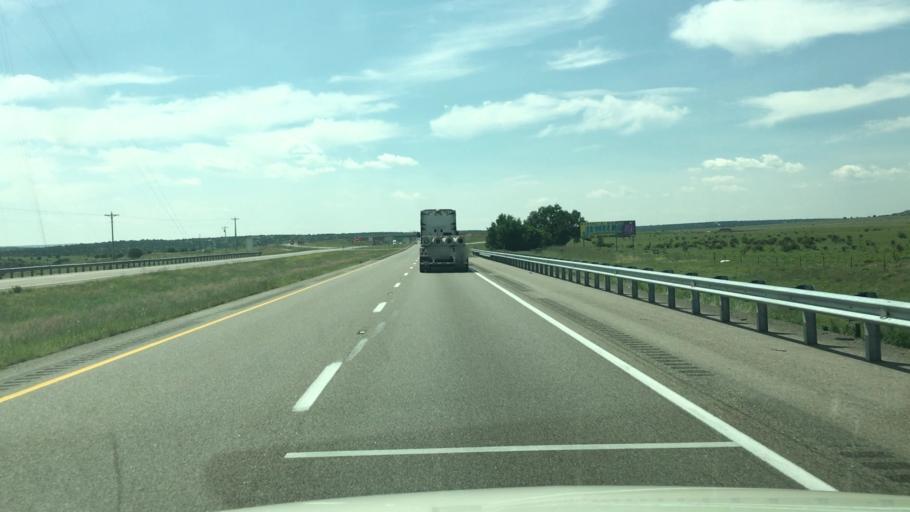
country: US
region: New Mexico
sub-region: San Miguel County
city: Las Vegas
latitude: 34.9913
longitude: -105.2865
